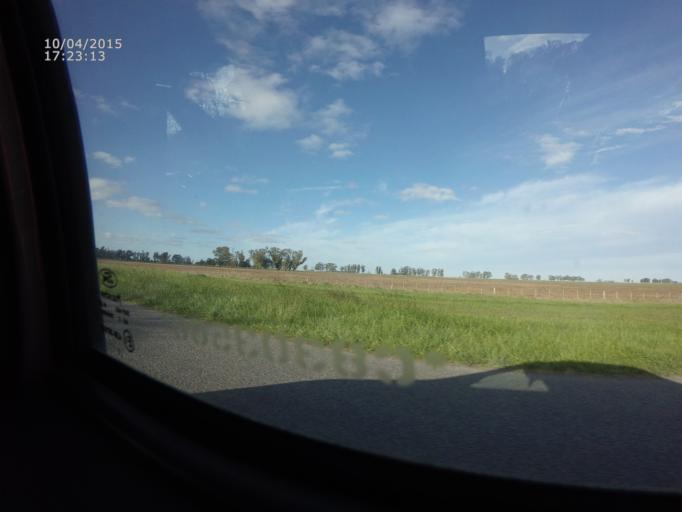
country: AR
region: Buenos Aires
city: Maipu
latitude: -37.1032
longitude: -57.8267
